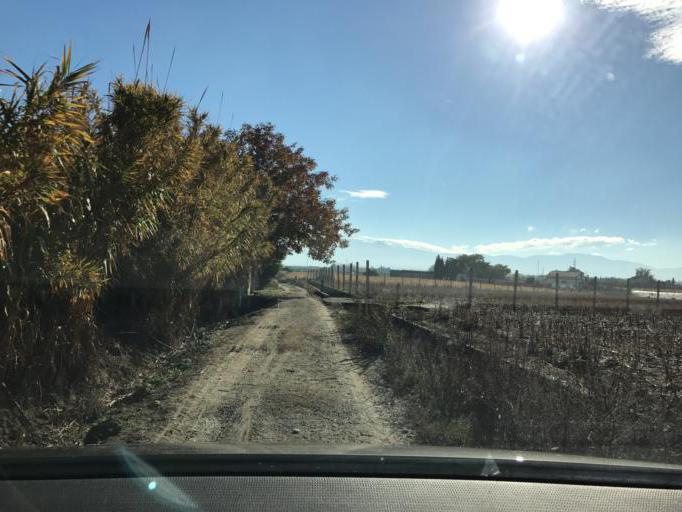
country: ES
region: Andalusia
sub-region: Provincia de Granada
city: Cullar-Vega
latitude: 37.1620
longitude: -3.6574
